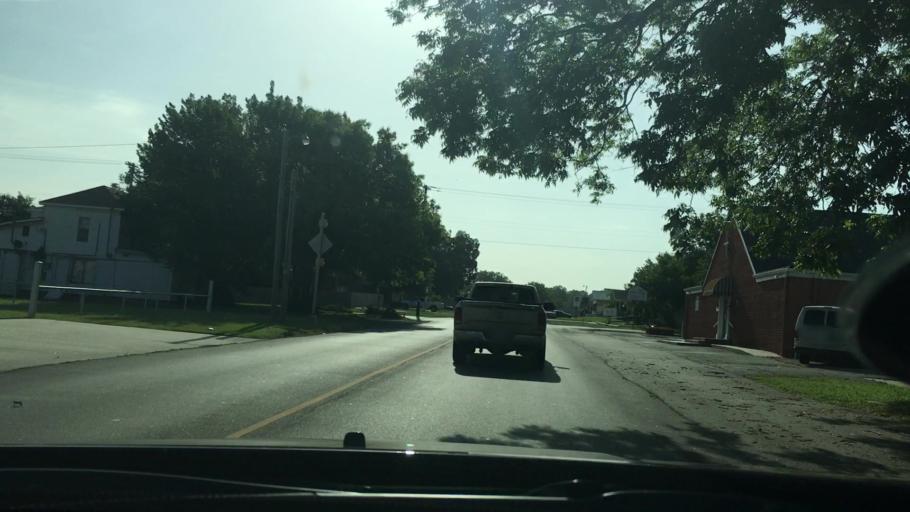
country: US
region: Oklahoma
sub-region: Pontotoc County
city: Ada
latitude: 34.7734
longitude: -96.6732
